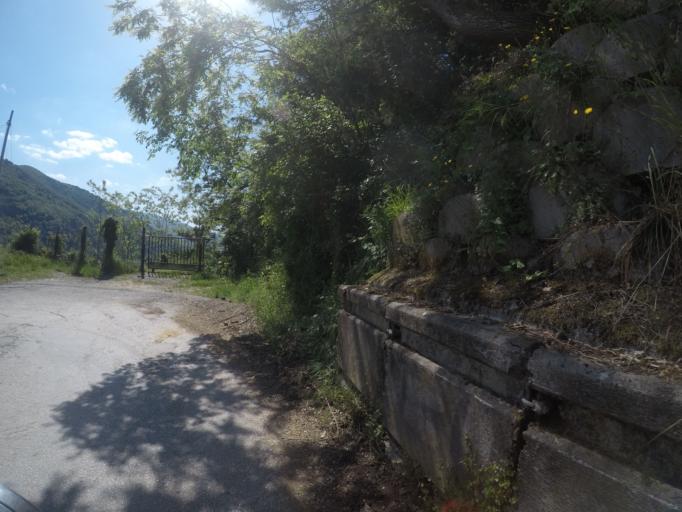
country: IT
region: Tuscany
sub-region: Provincia di Massa-Carrara
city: Massa
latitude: 44.0647
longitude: 10.1091
